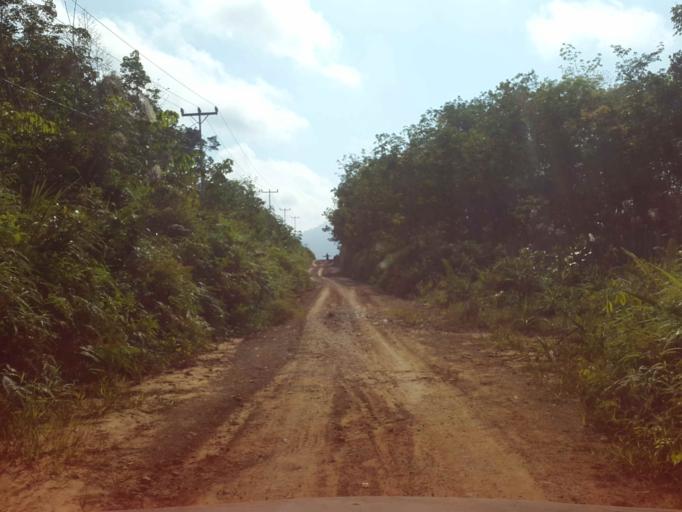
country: MY
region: Sarawak
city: Simanggang
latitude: 0.9421
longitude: 111.0972
